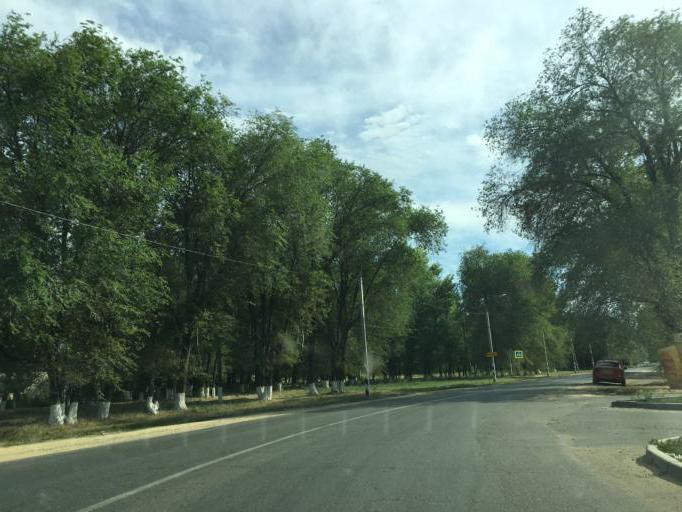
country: RU
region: Krasnodarskiy
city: Kushchevskaya
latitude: 46.5439
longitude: 39.6219
